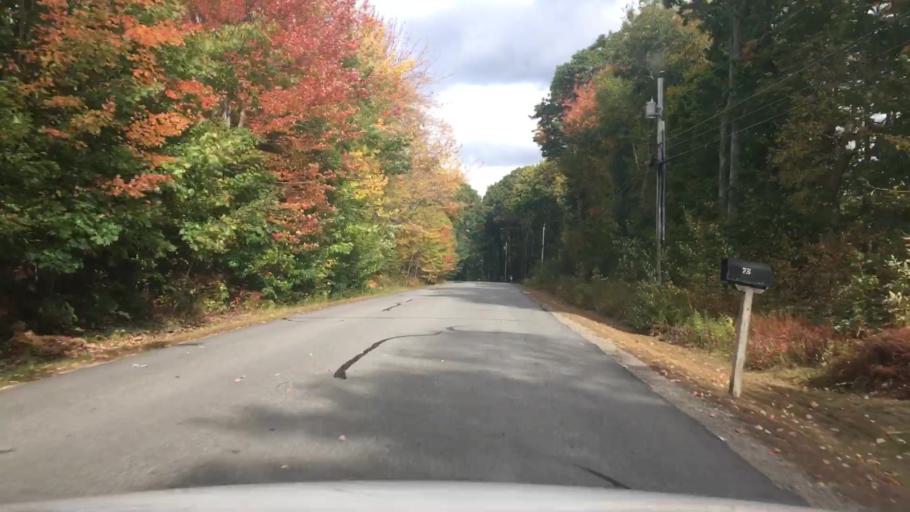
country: US
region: Maine
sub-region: Knox County
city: Camden
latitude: 44.2199
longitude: -69.1017
